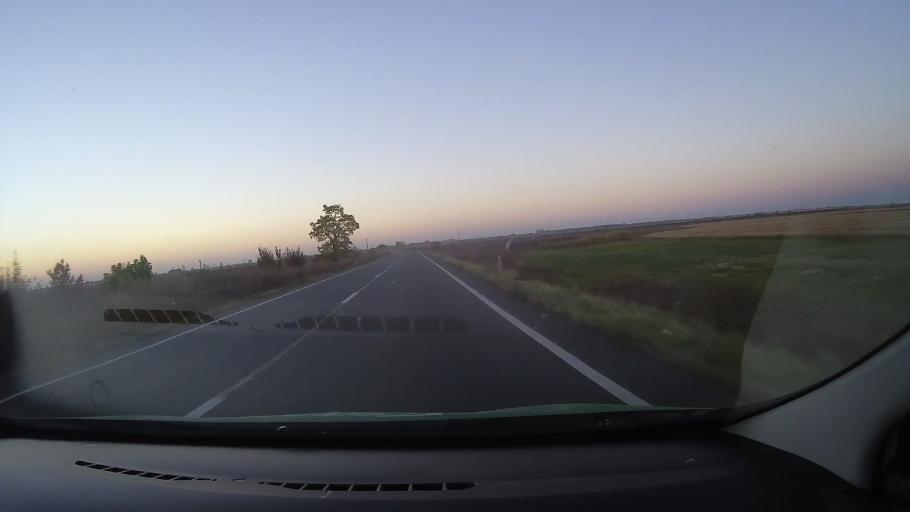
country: RO
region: Bihor
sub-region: Comuna Tarcea
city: Tarcea
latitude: 47.4420
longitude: 22.1913
